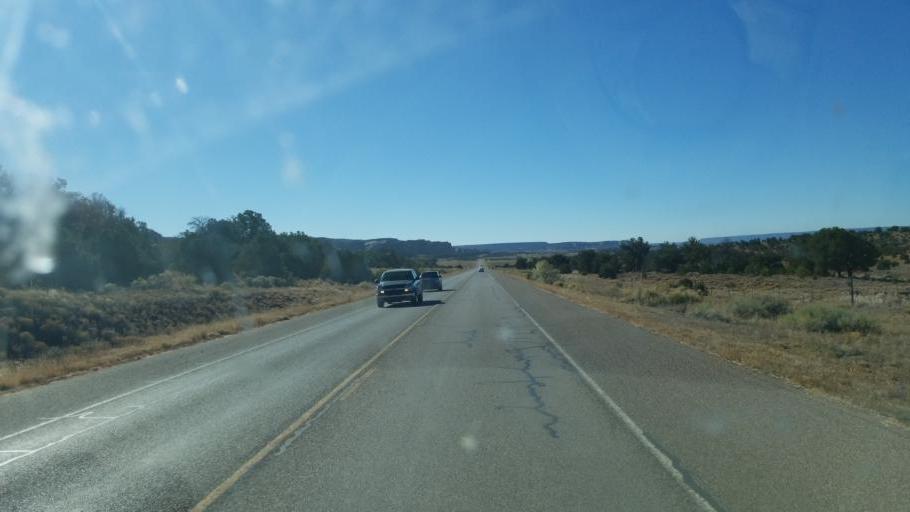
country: US
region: Arizona
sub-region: Apache County
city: Fort Defiance
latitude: 35.7944
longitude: -109.0376
